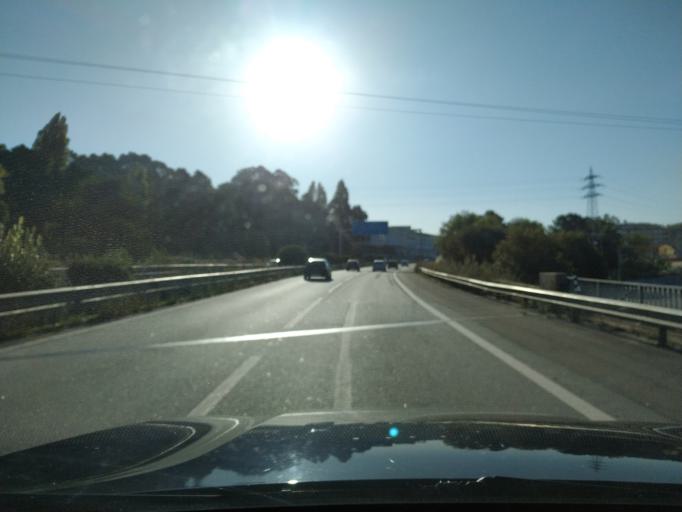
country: PT
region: Porto
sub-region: Vila Nova de Gaia
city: Vilar de Andorinho
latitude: 41.1100
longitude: -8.6070
